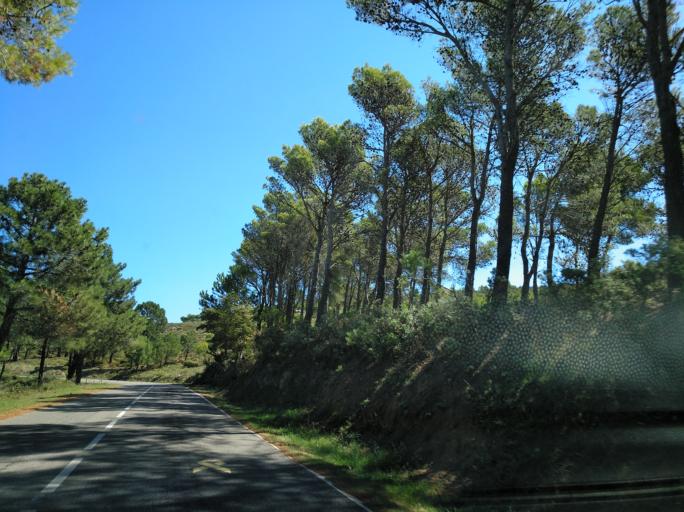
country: ES
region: Catalonia
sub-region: Provincia de Girona
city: Llanca
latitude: 42.3269
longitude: 3.1517
